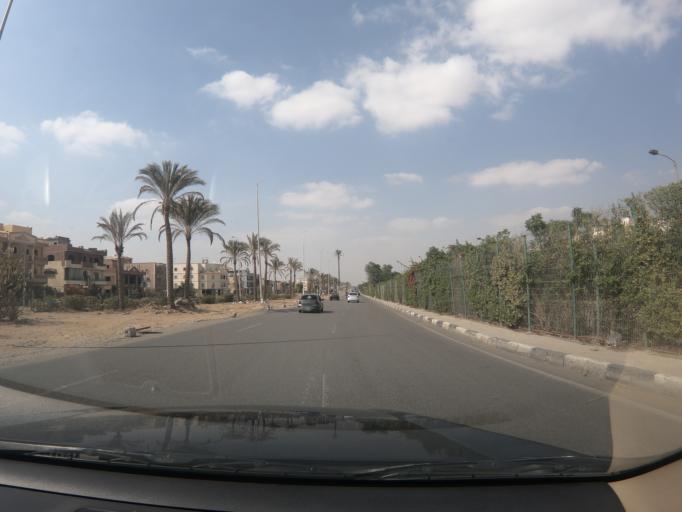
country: EG
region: Muhafazat al Qalyubiyah
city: Al Khankah
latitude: 30.0558
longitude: 31.4751
